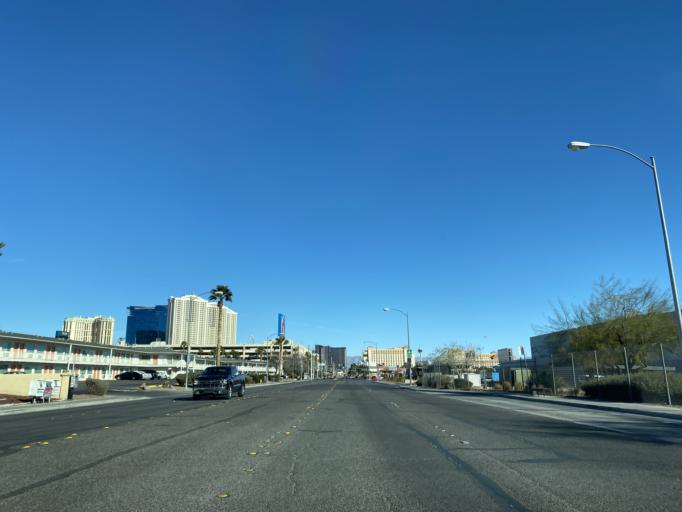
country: US
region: Nevada
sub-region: Clark County
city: Paradise
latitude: 36.0983
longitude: -115.1638
